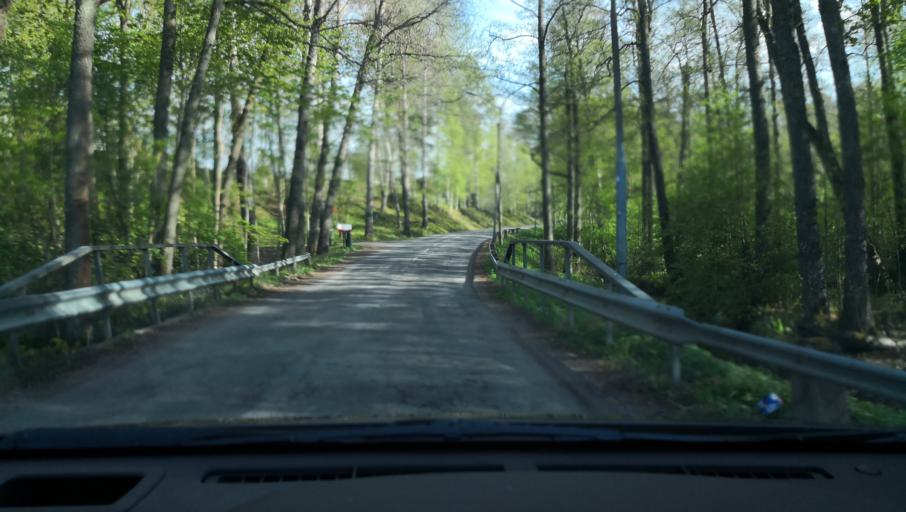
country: SE
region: OErebro
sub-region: Askersunds Kommun
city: Asbro
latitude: 58.9815
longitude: 15.0581
